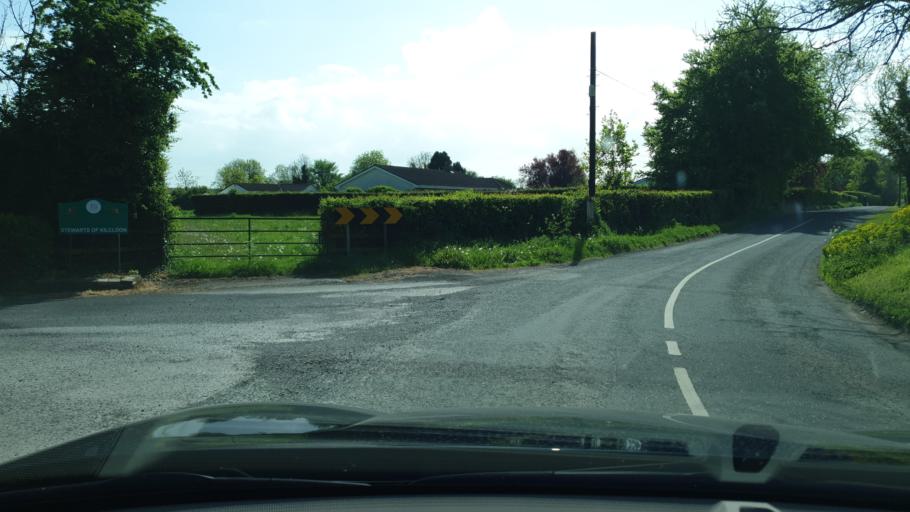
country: IE
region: Leinster
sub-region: Kildare
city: Maynooth
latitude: 53.4340
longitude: -6.5661
